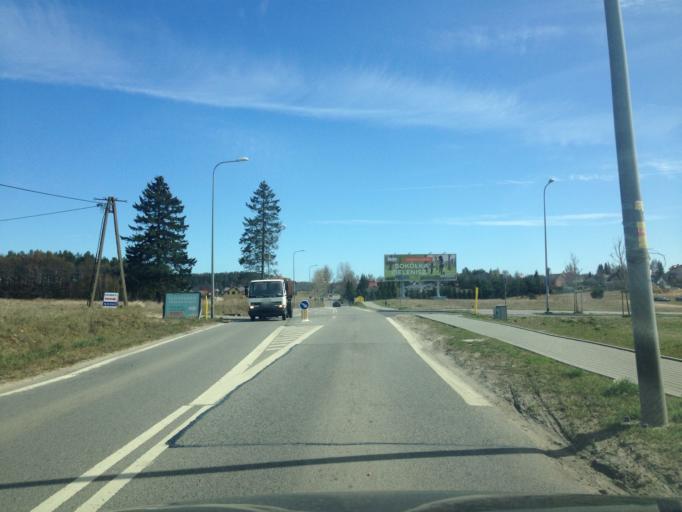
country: PL
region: Pomeranian Voivodeship
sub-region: Powiat kartuski
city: Chwaszczyno
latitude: 54.4879
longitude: 18.4282
